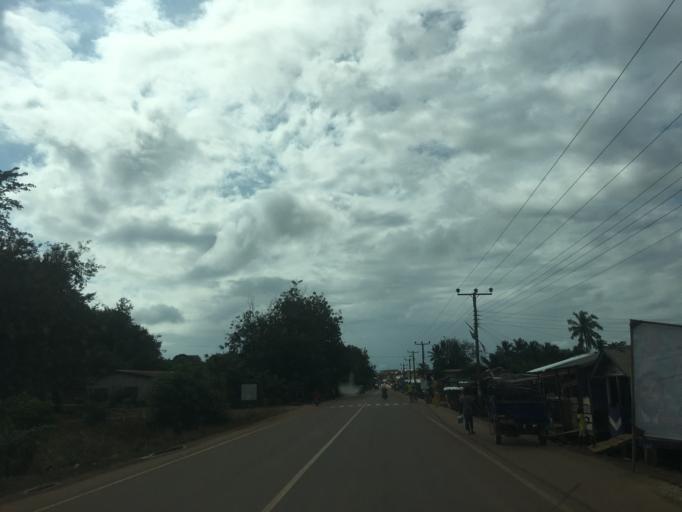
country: GH
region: Western
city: Wassa-Akropong
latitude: 5.8018
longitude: -2.4303
